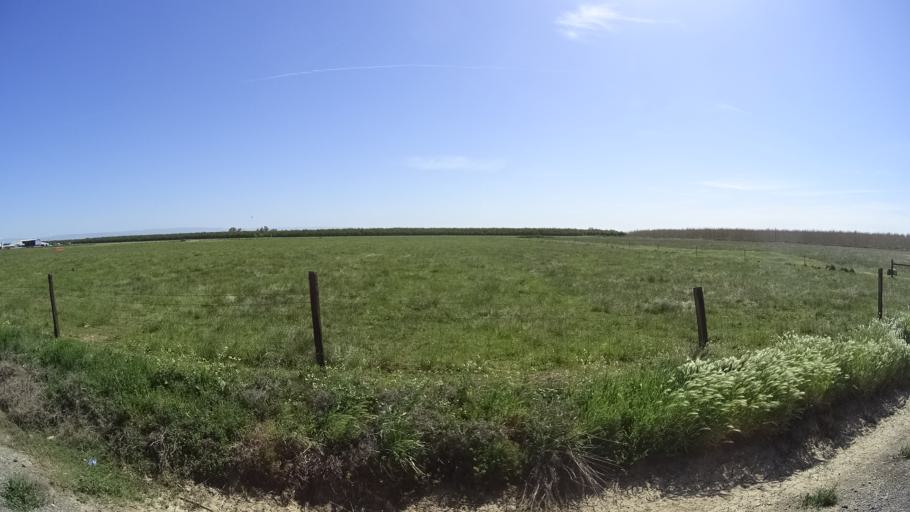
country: US
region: California
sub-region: Glenn County
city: Hamilton City
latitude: 39.6545
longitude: -122.1036
